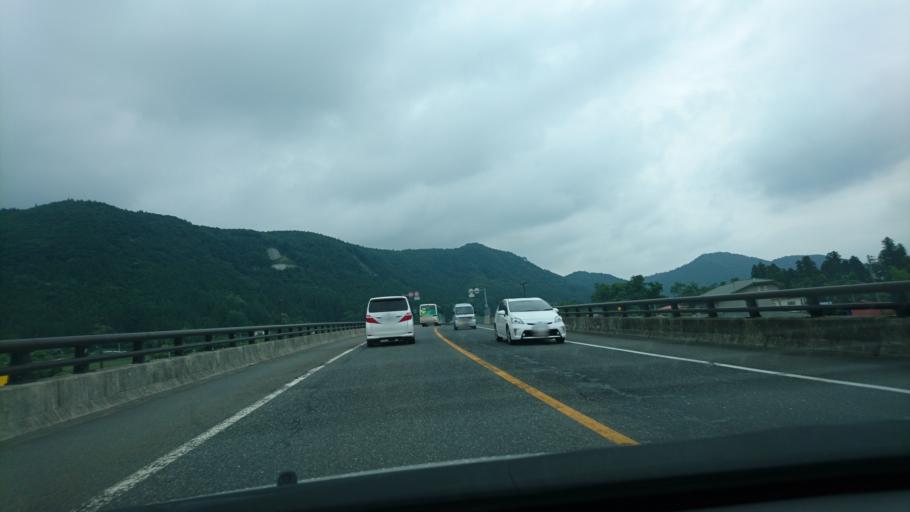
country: JP
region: Miyagi
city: Furukawa
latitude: 38.7338
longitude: 140.7840
